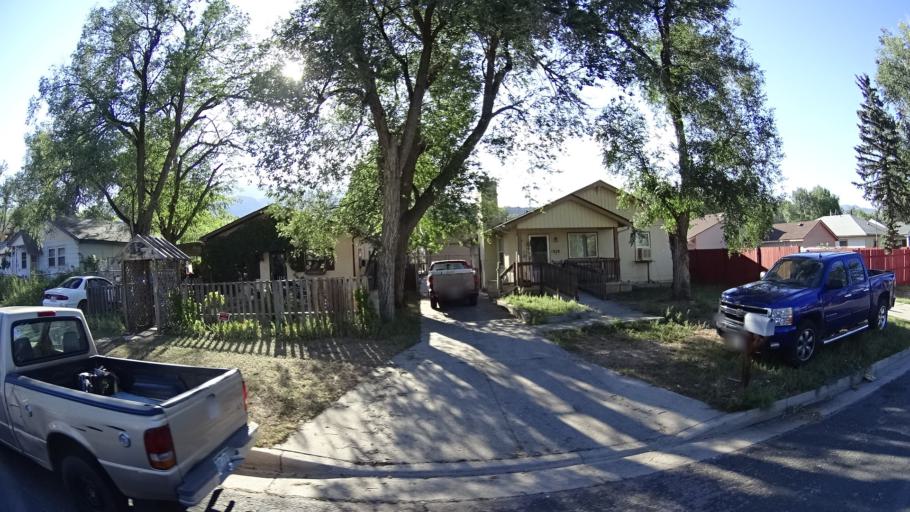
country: US
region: Colorado
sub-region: El Paso County
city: Colorado Springs
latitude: 38.8380
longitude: -104.8657
